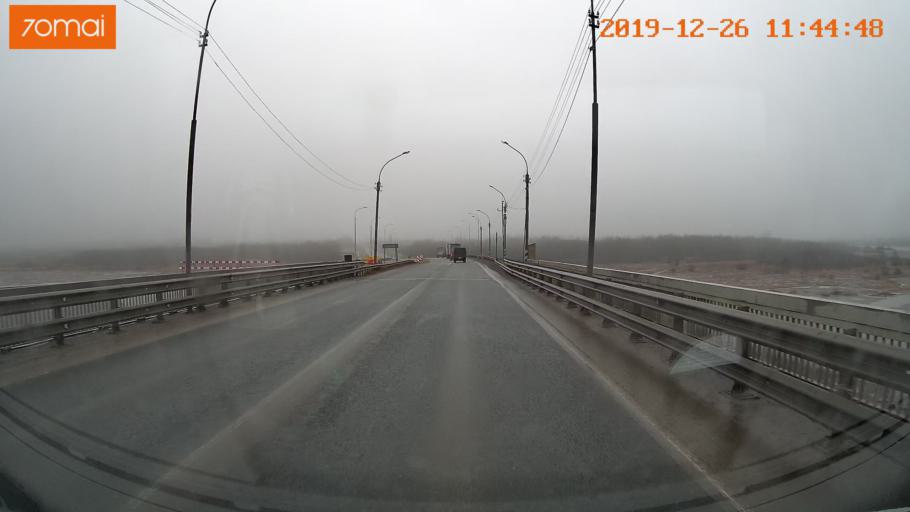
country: RU
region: Vologda
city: Sheksna
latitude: 59.2139
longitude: 38.4935
